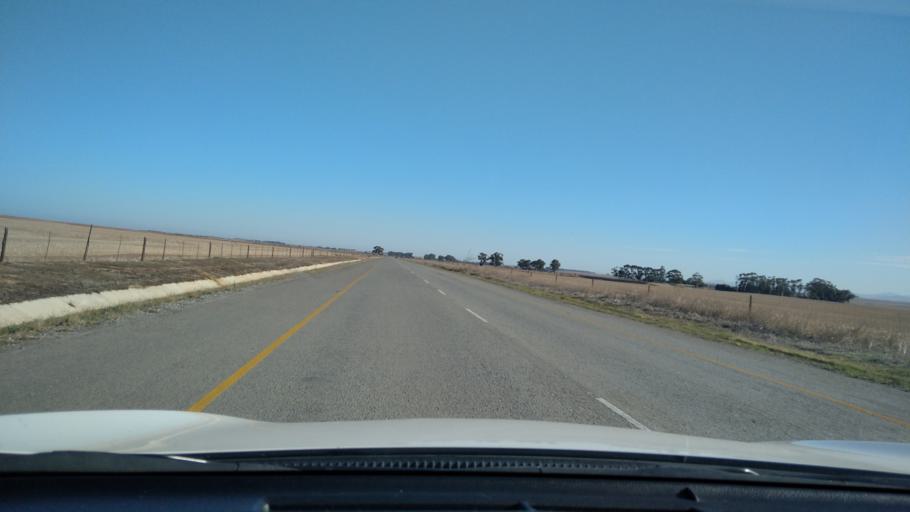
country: ZA
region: Western Cape
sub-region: West Coast District Municipality
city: Moorreesburg
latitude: -33.2927
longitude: 18.6097
